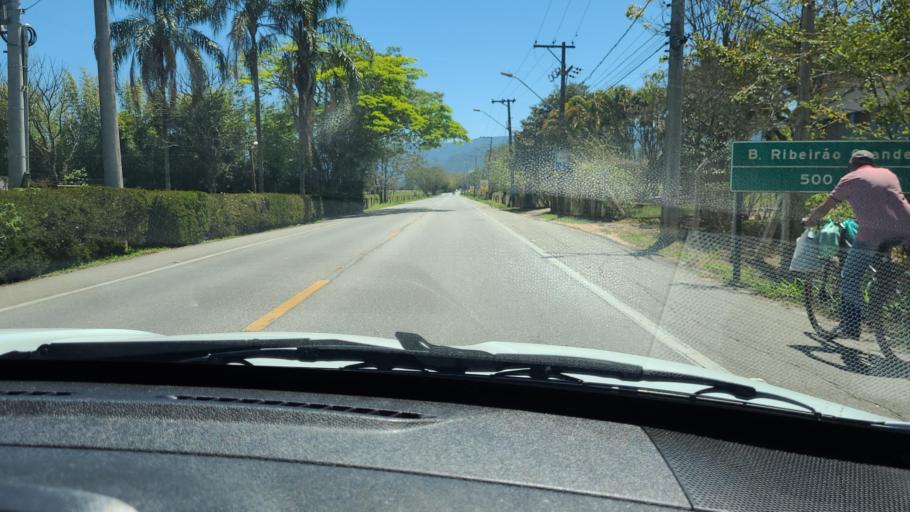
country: BR
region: Sao Paulo
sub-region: Pindamonhangaba
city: Pindamonhangaba
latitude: -22.9059
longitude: -45.4782
